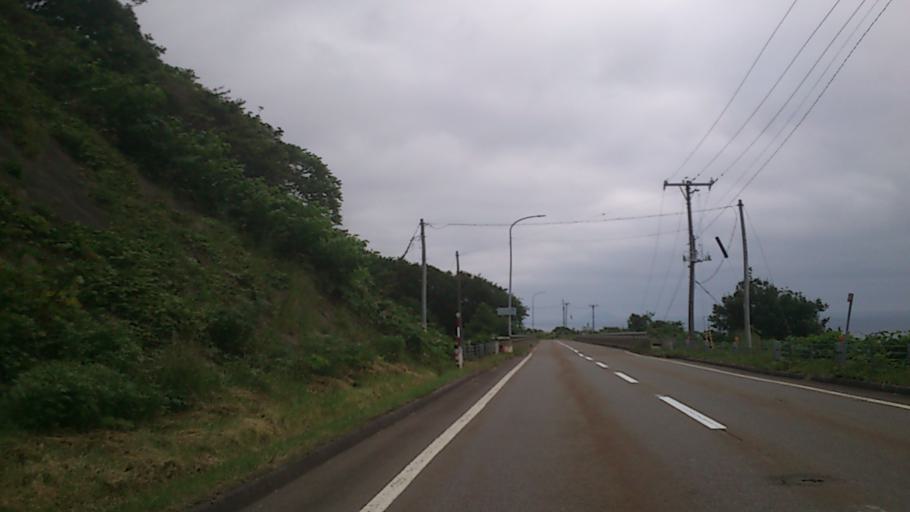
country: JP
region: Hokkaido
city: Kamiiso
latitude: 41.6809
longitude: 140.0097
